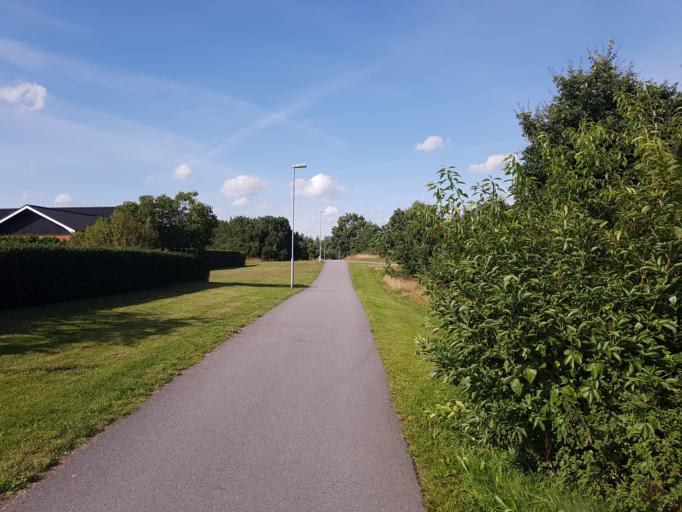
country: SE
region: Skane
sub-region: Sjobo Kommun
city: Sjoebo
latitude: 55.6400
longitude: 13.7000
